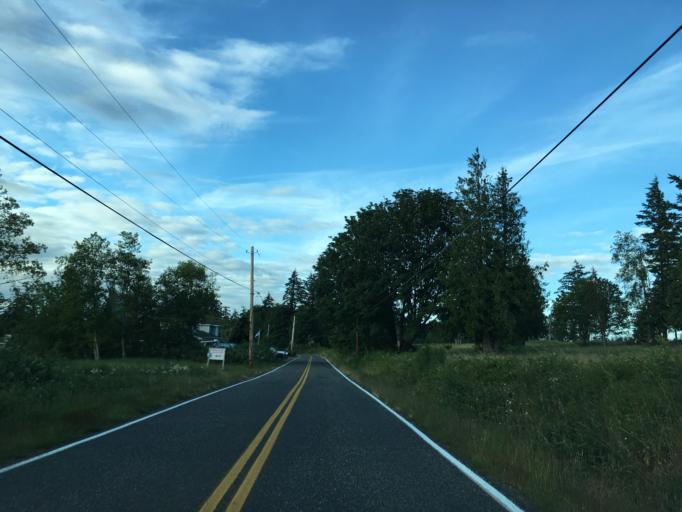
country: CA
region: British Columbia
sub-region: Greater Vancouver Regional District
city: White Rock
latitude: 48.9590
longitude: -122.8073
